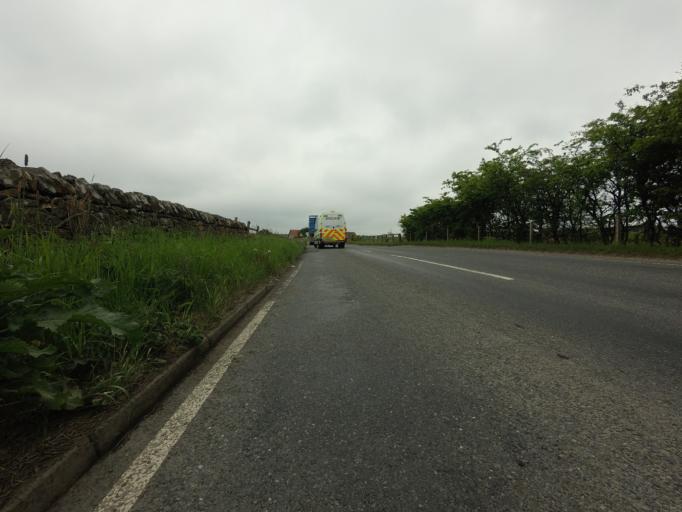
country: GB
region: Scotland
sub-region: Fife
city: Townhill
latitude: 56.1213
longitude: -3.4390
